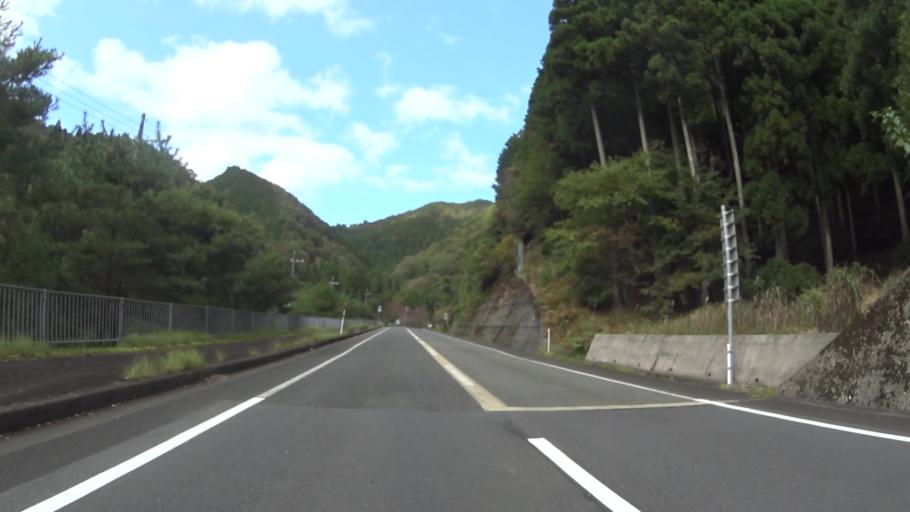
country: JP
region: Hyogo
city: Toyooka
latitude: 35.5215
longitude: 134.9884
